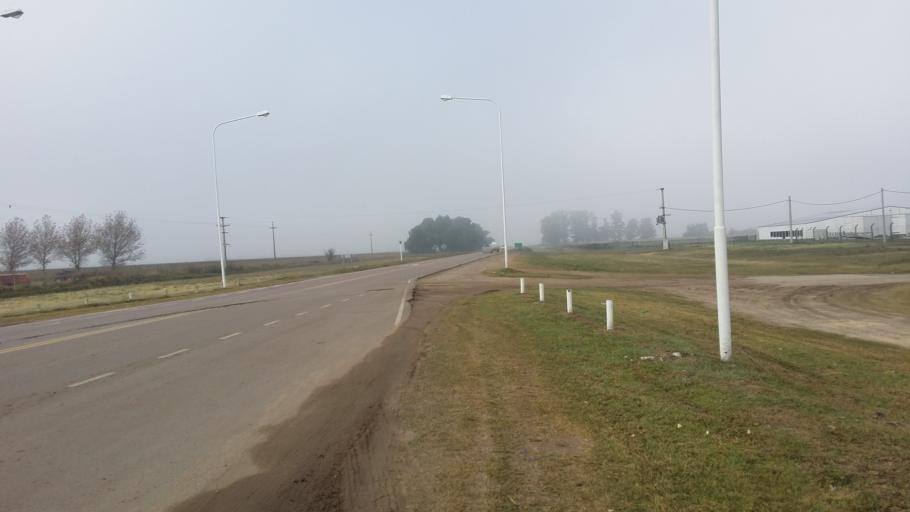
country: AR
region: La Pampa
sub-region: Departamento de Quemu Quemu
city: Quemu Quemu
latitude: -36.0648
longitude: -63.5845
